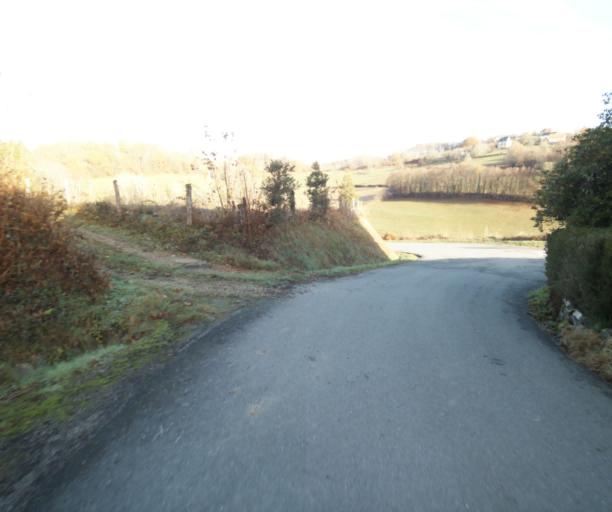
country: FR
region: Limousin
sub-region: Departement de la Correze
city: Laguenne
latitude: 45.2565
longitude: 1.8010
